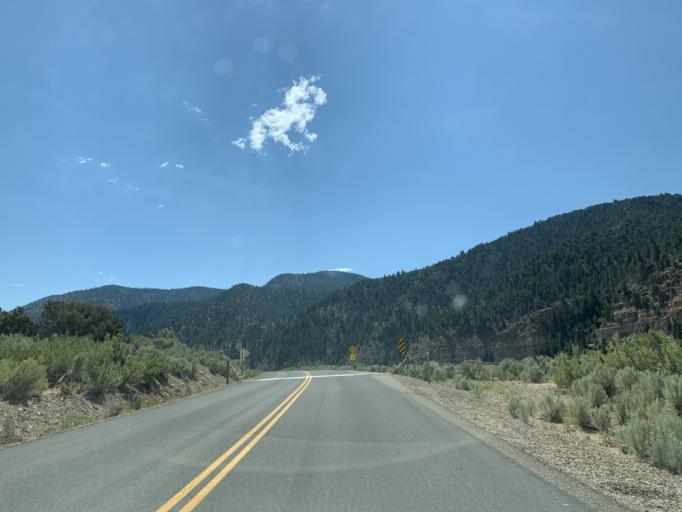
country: US
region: Utah
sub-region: Carbon County
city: East Carbon City
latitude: 39.7784
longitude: -110.4390
